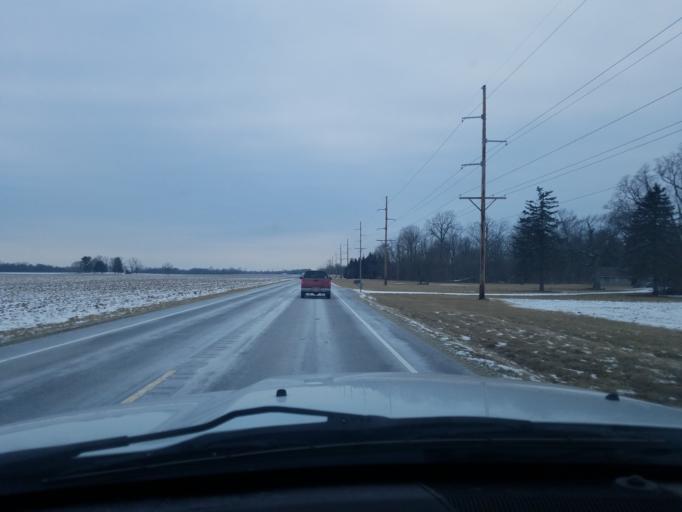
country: US
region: Indiana
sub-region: Randolph County
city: Farmland
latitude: 40.1715
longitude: -85.0890
